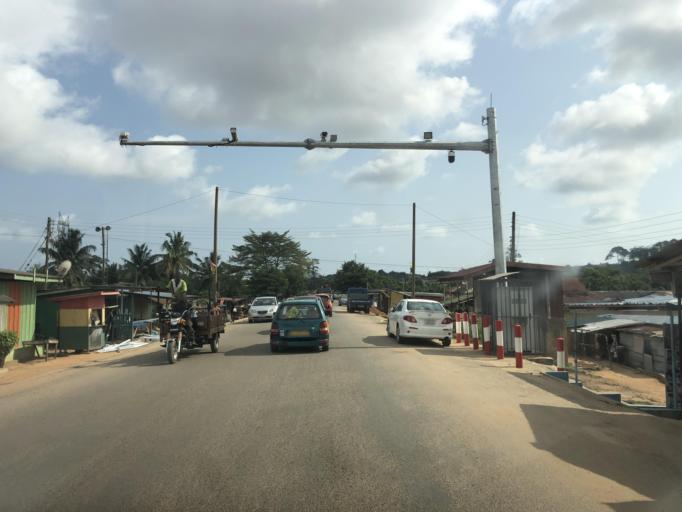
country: GH
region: Central
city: Cape Coast
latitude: 5.1493
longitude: -1.2882
